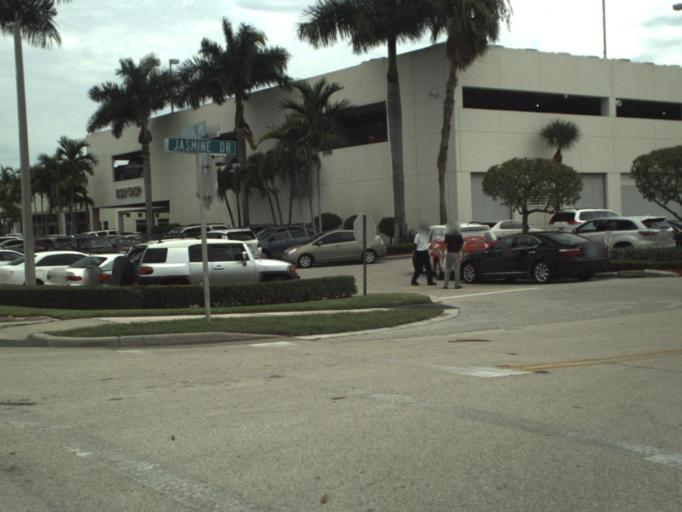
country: US
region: Florida
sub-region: Palm Beach County
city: Lake Park
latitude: 26.8019
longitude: -80.0550
